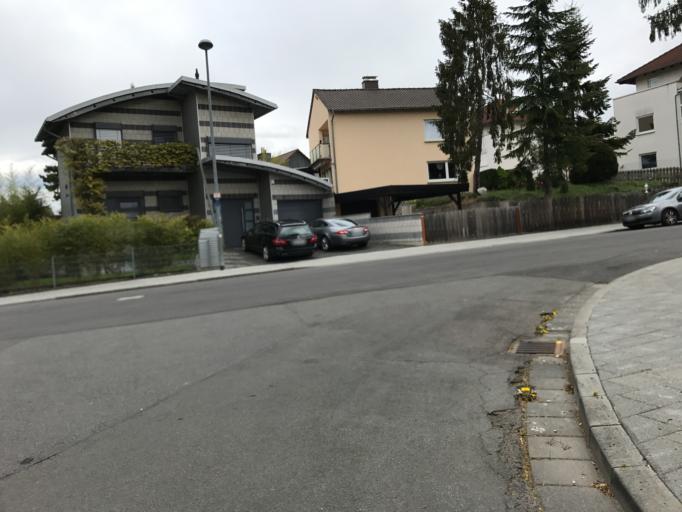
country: DE
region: Rheinland-Pfalz
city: Mainz
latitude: 49.9836
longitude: 8.2546
